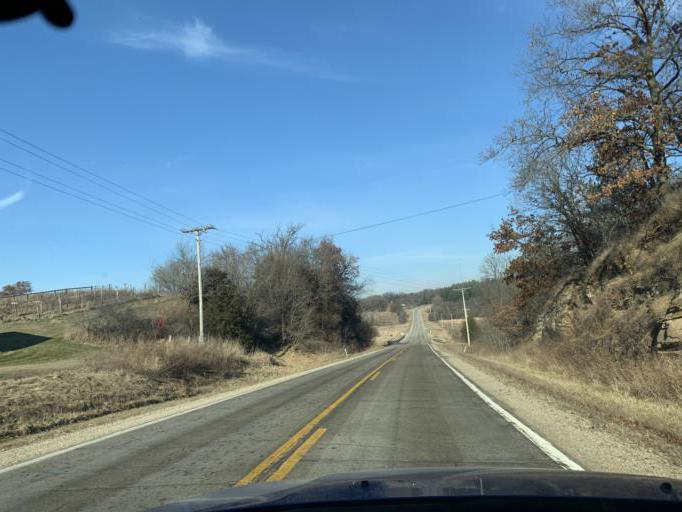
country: US
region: Wisconsin
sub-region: Green County
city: New Glarus
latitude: 42.7840
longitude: -89.8613
